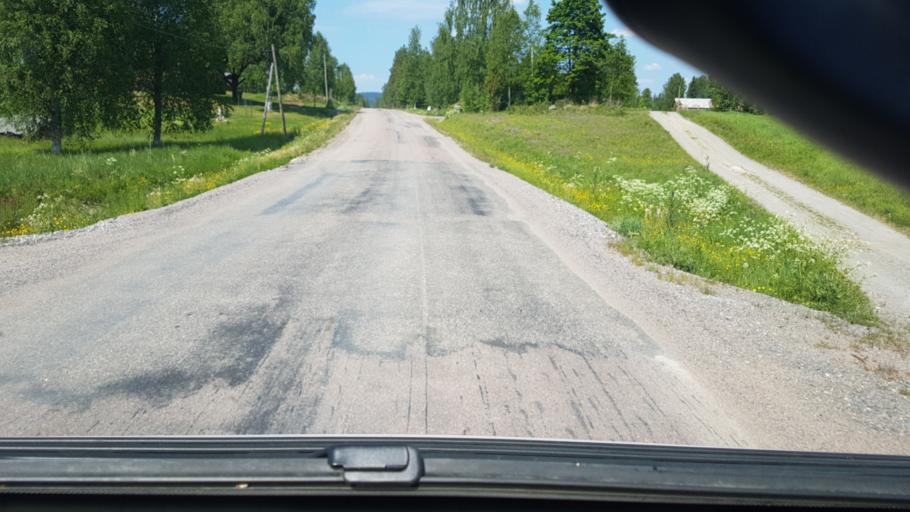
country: SE
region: Vaermland
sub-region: Eda Kommun
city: Charlottenberg
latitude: 59.9481
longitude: 12.5185
